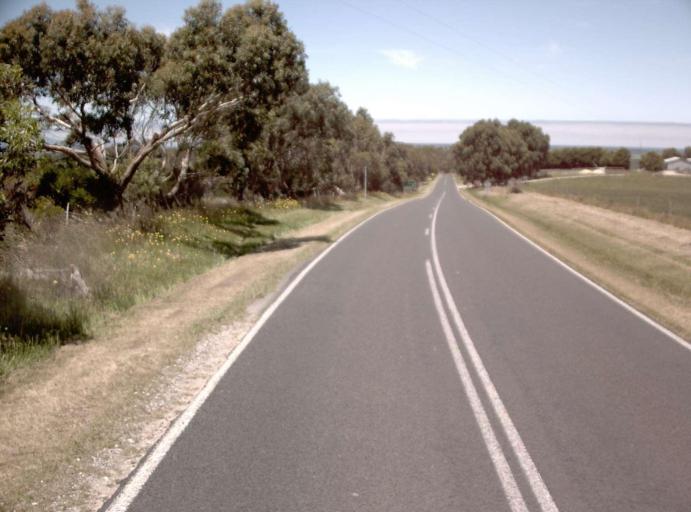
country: AU
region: Victoria
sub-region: Bass Coast
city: North Wonthaggi
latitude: -38.7472
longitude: 146.1341
